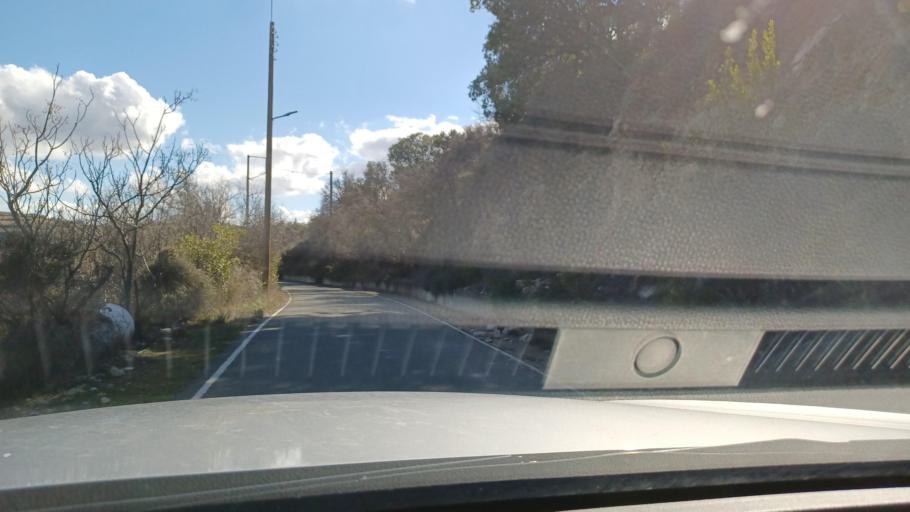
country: CY
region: Limassol
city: Pachna
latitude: 34.8234
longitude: 32.8048
